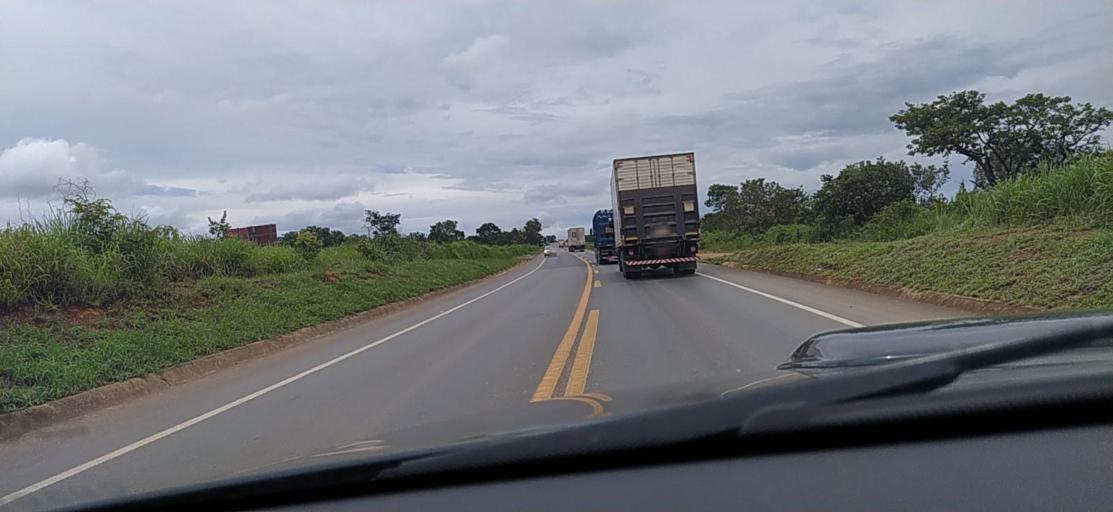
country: BR
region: Minas Gerais
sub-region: Curvelo
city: Curvelo
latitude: -18.7234
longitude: -44.4419
